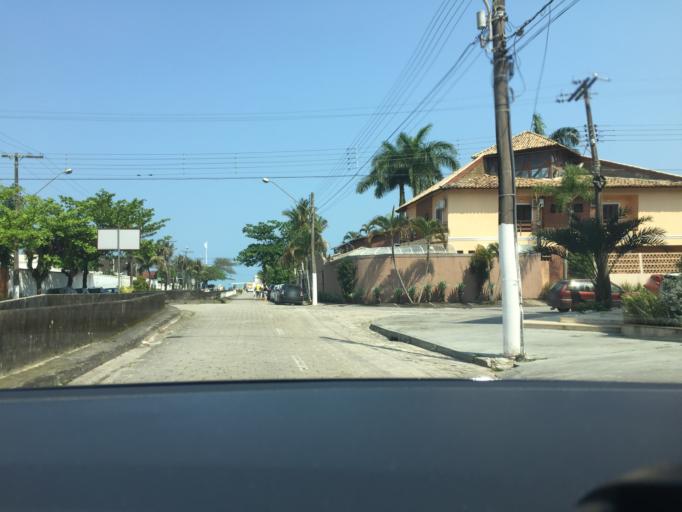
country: BR
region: Sao Paulo
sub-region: Guaruja
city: Guaruja
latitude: -23.9836
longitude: -46.2212
